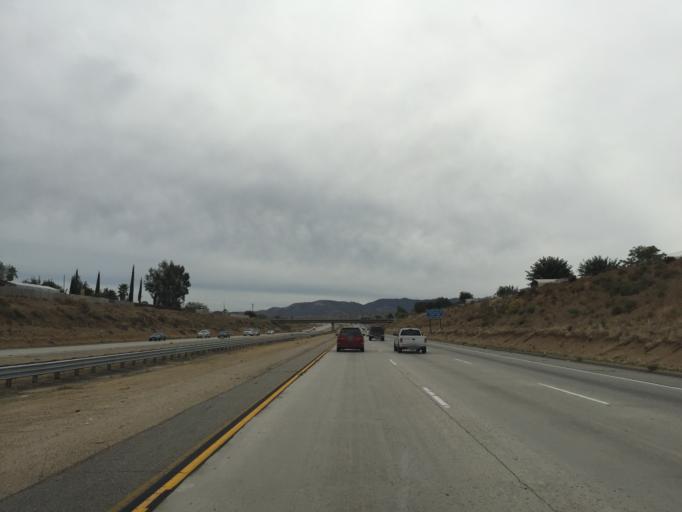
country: US
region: California
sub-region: Los Angeles County
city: Desert View Highlands
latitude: 34.6197
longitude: -118.1534
